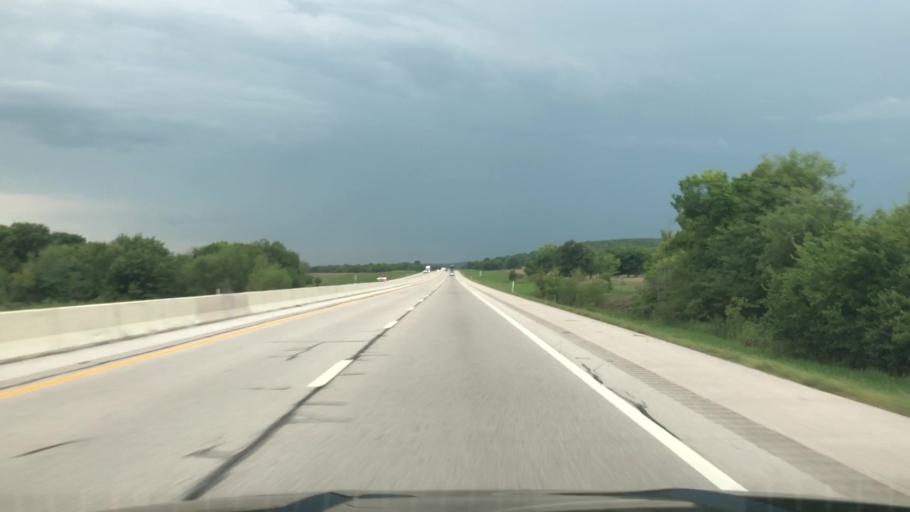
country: US
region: Oklahoma
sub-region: Rogers County
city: Bushyhead
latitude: 36.3741
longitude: -95.4407
